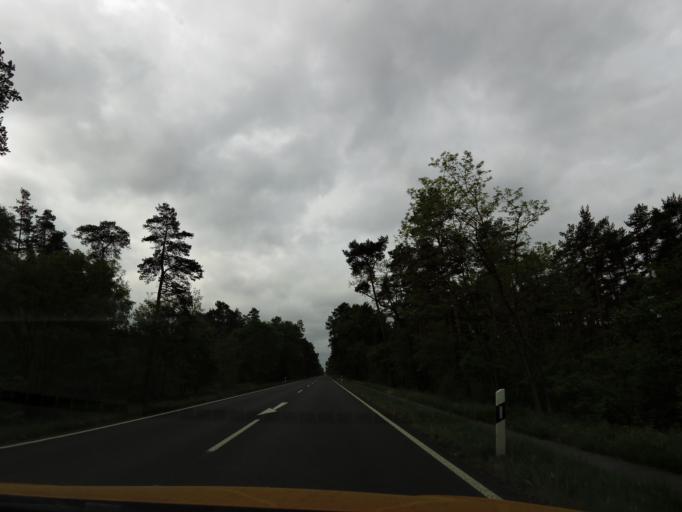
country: DE
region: Brandenburg
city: Treuenbrietzen
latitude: 52.1451
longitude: 12.9193
